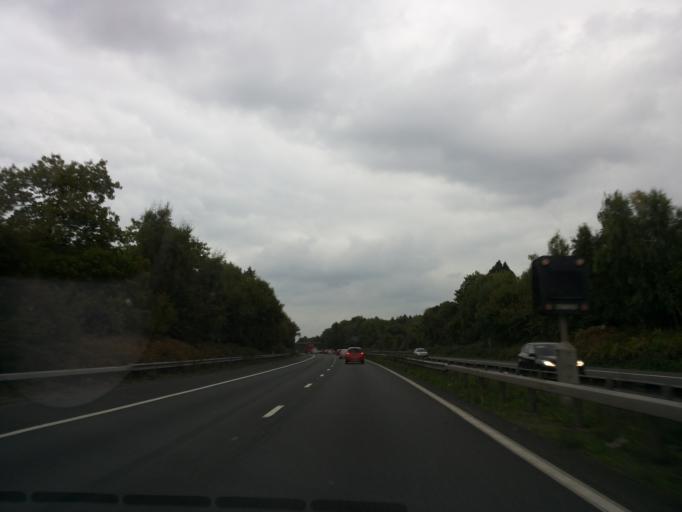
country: GB
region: England
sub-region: Kent
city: Sittingbourne
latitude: 51.2981
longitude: 0.7398
